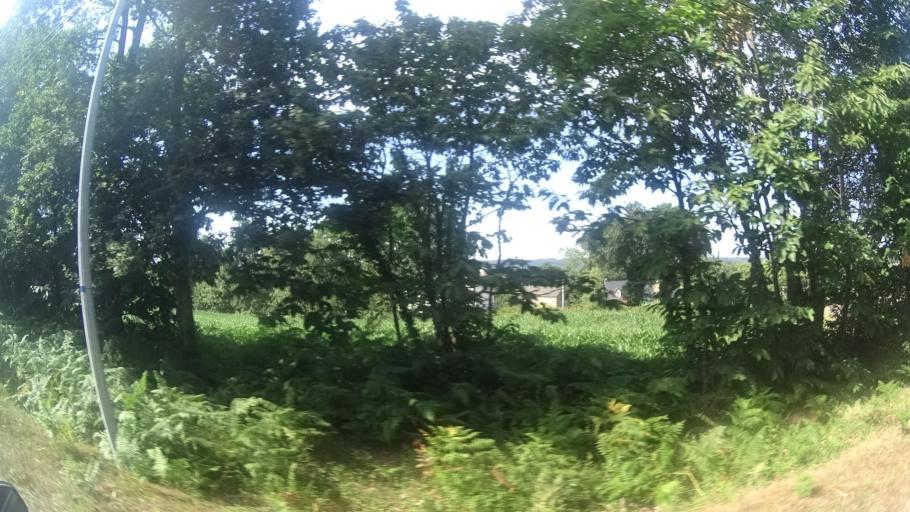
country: FR
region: Brittany
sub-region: Departement du Morbihan
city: Beganne
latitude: 47.5975
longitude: -2.2534
